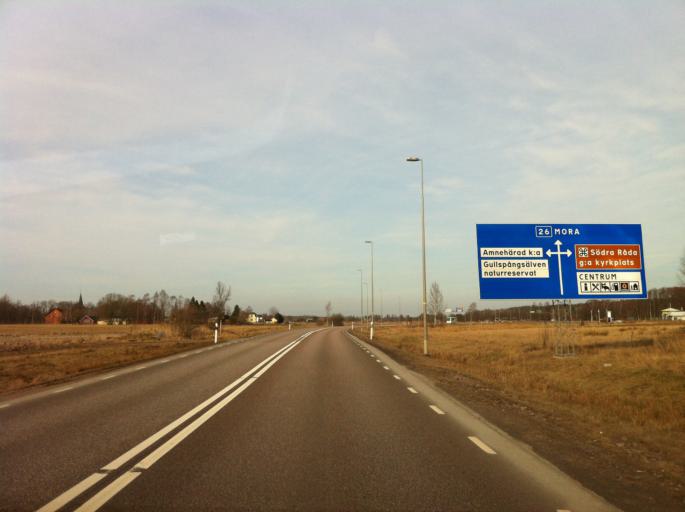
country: SE
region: Vaestra Goetaland
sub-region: Gullspangs Kommun
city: Gullspang
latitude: 58.9837
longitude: 14.0881
